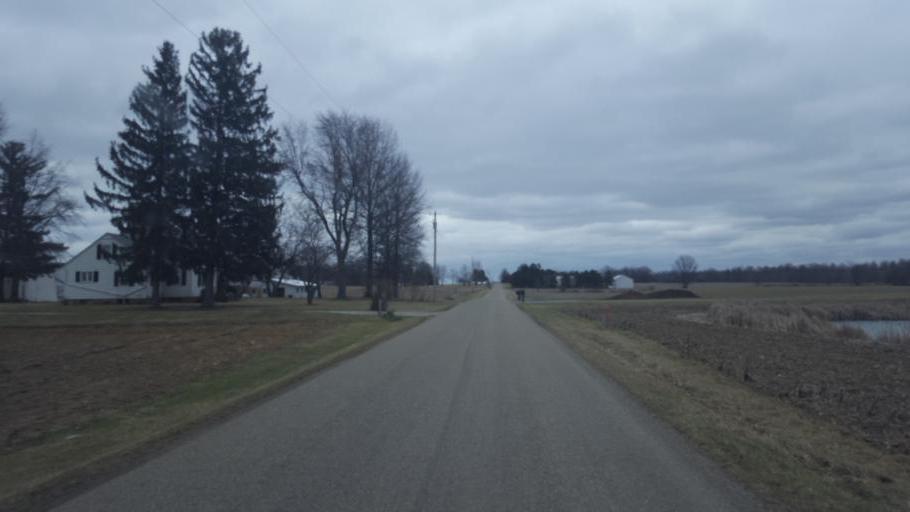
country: US
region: Ohio
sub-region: Richland County
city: Lexington
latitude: 40.6633
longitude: -82.6794
